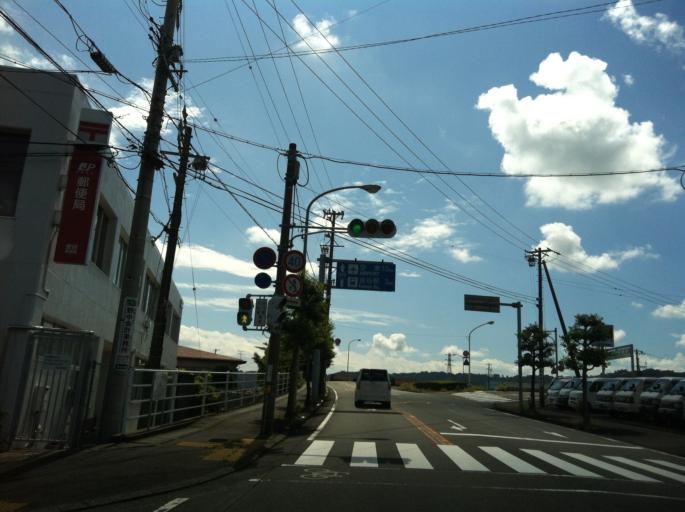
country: JP
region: Shizuoka
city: Kanaya
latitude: 34.8345
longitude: 138.1259
